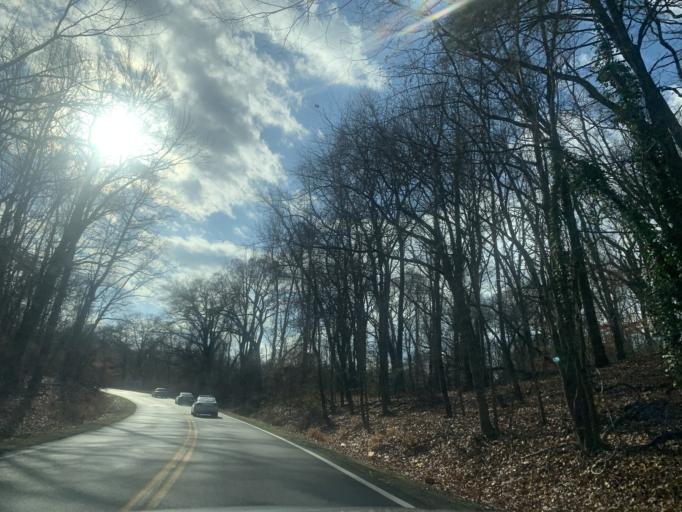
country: US
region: Maryland
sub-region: Prince George's County
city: Coral Hills
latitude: 38.8785
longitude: -76.9490
